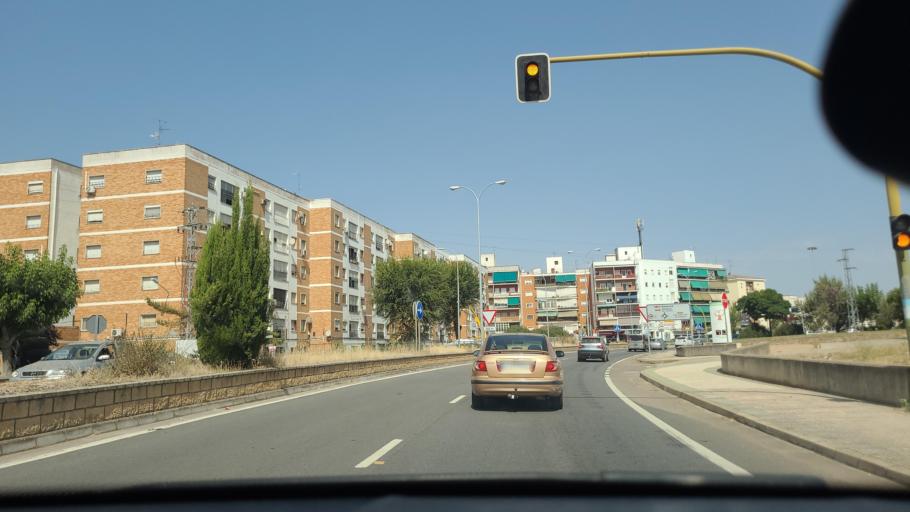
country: ES
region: Extremadura
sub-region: Provincia de Badajoz
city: Zafra
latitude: 38.4228
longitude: -6.4110
